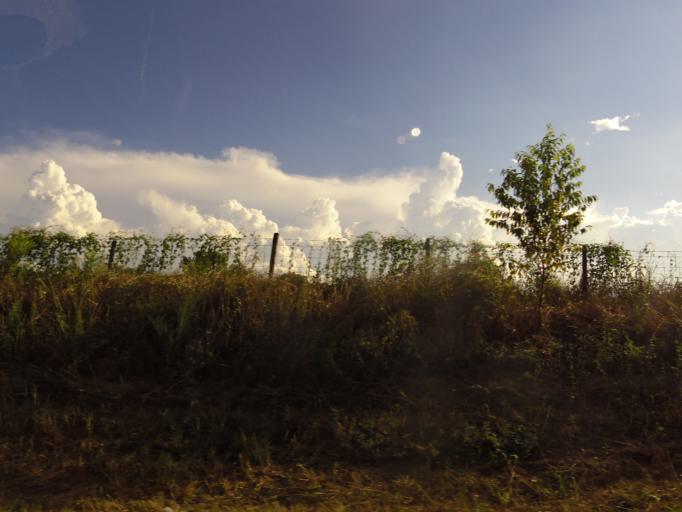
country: US
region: Georgia
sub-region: Brooks County
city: Quitman
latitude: 30.7771
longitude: -83.6044
